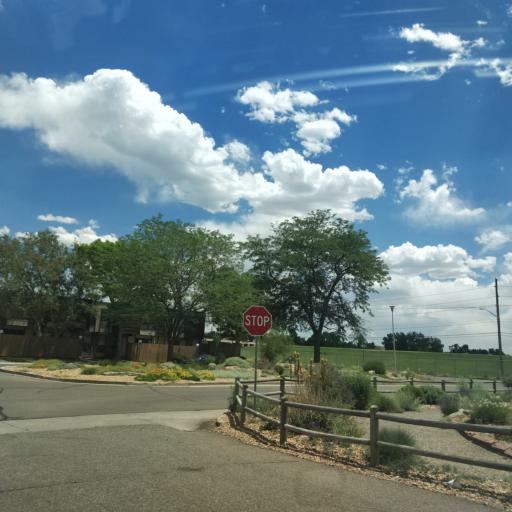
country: US
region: Colorado
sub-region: Jefferson County
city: Lakewood
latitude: 39.6826
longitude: -105.1039
